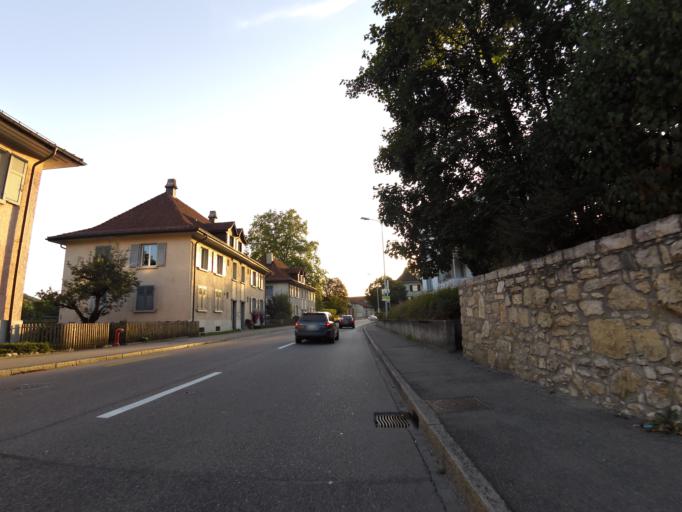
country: CH
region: Aargau
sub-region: Bezirk Aarau
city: Aarau
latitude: 47.3963
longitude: 8.0384
